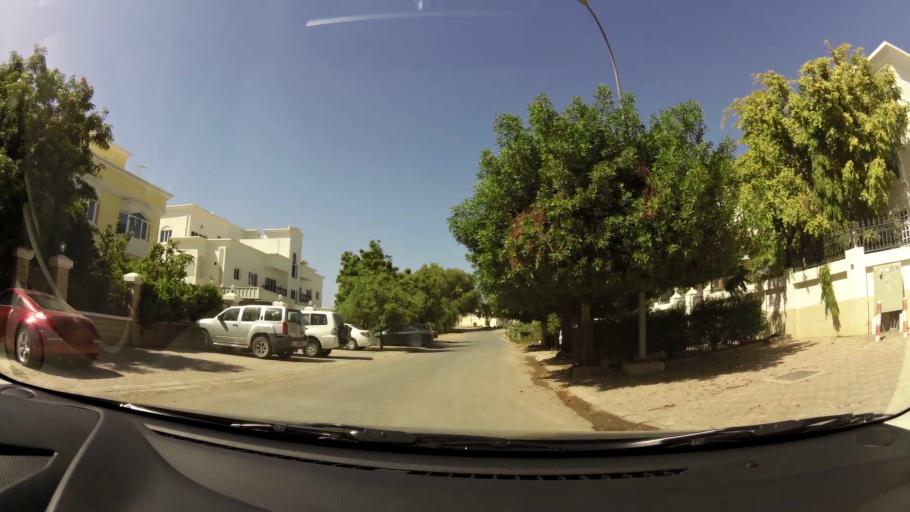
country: OM
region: Muhafazat Masqat
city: Bawshar
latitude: 23.6022
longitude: 58.3775
